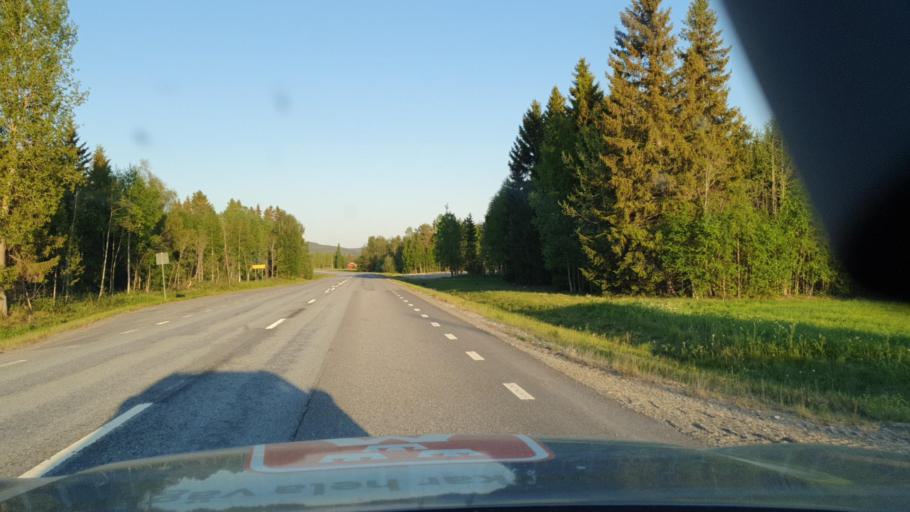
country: SE
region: Vaesternorrland
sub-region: Solleftea Kommun
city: Solleftea
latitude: 63.3260
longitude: 17.1590
